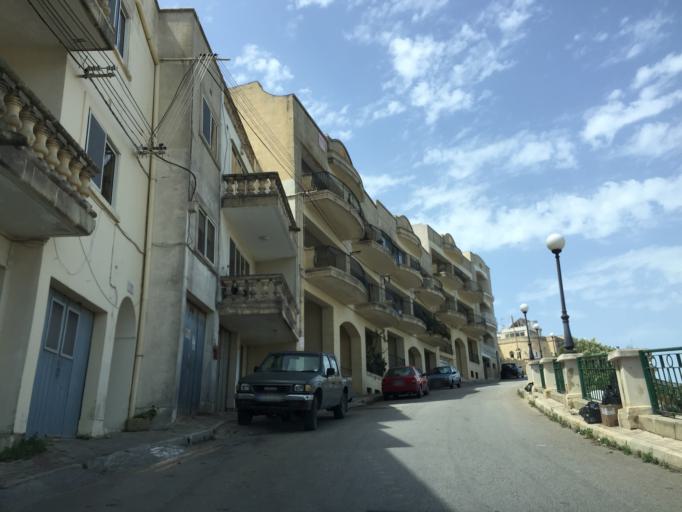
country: MT
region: In-Nadur
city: Nadur
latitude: 36.0377
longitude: 14.2861
